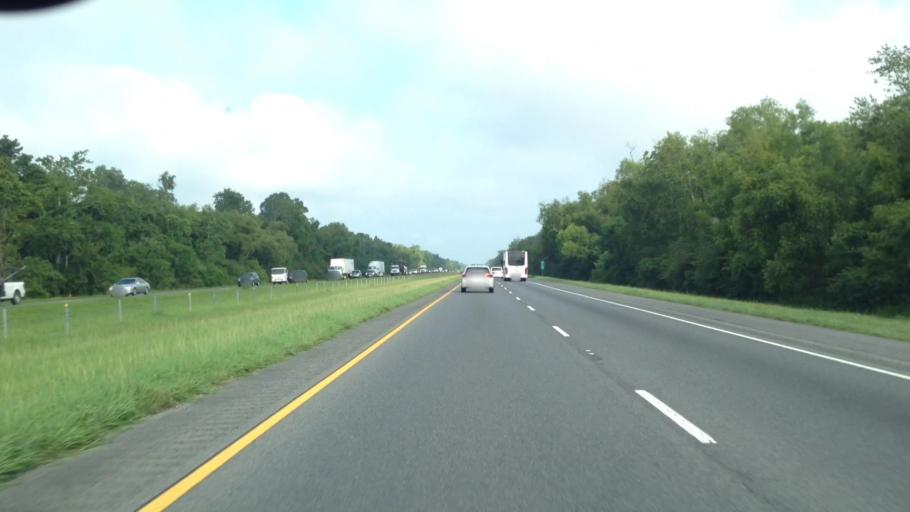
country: US
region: Louisiana
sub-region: Saint James Parish
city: Grand Point
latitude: 30.1339
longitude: -90.7267
